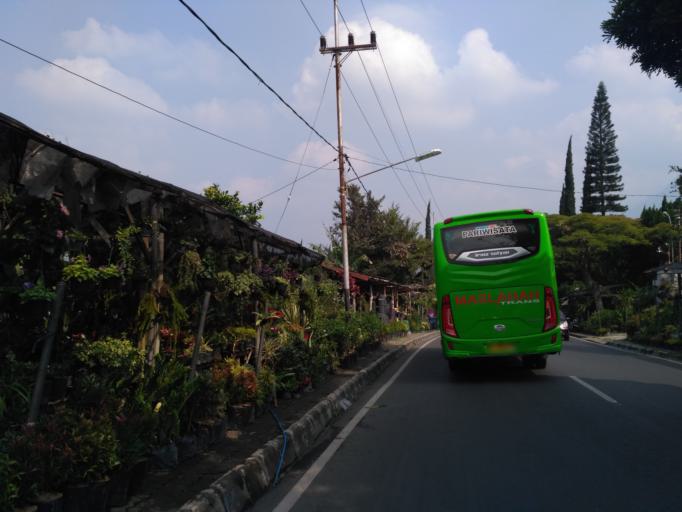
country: ID
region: East Java
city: Batu
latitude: -7.8545
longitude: 112.5273
